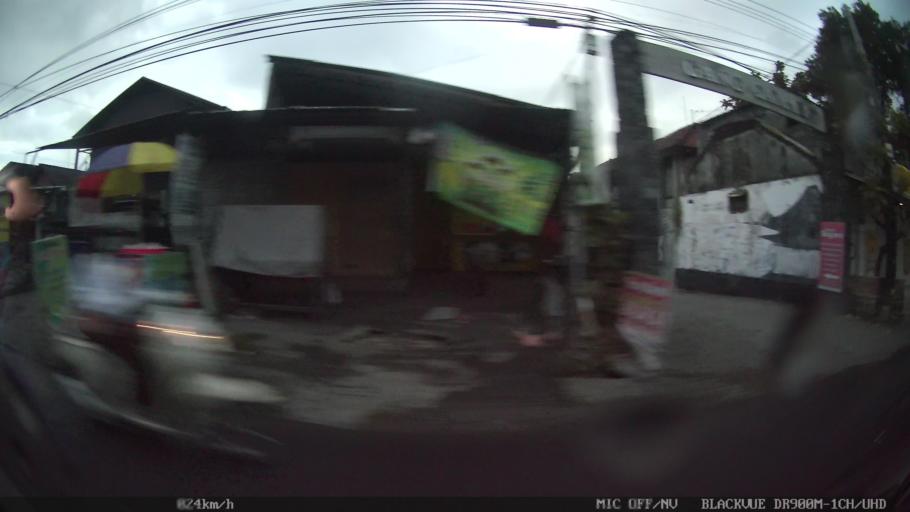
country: ID
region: Bali
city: Banjar Kertajiwa
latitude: -8.6274
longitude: 115.2639
